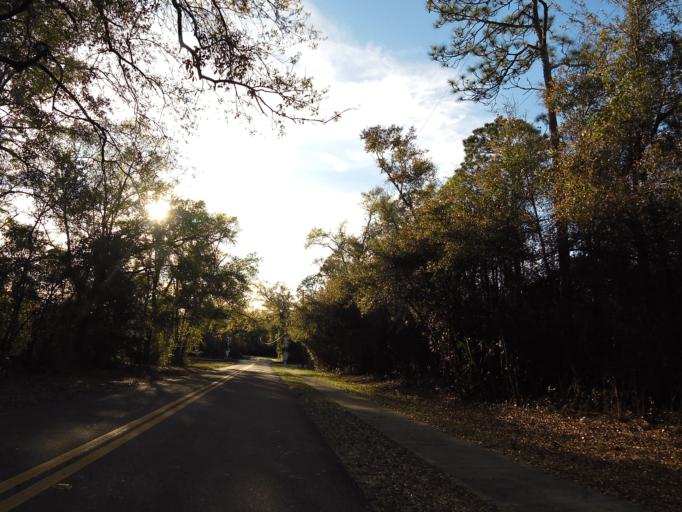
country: US
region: Florida
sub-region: Duval County
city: Jacksonville
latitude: 30.4394
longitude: -81.6093
